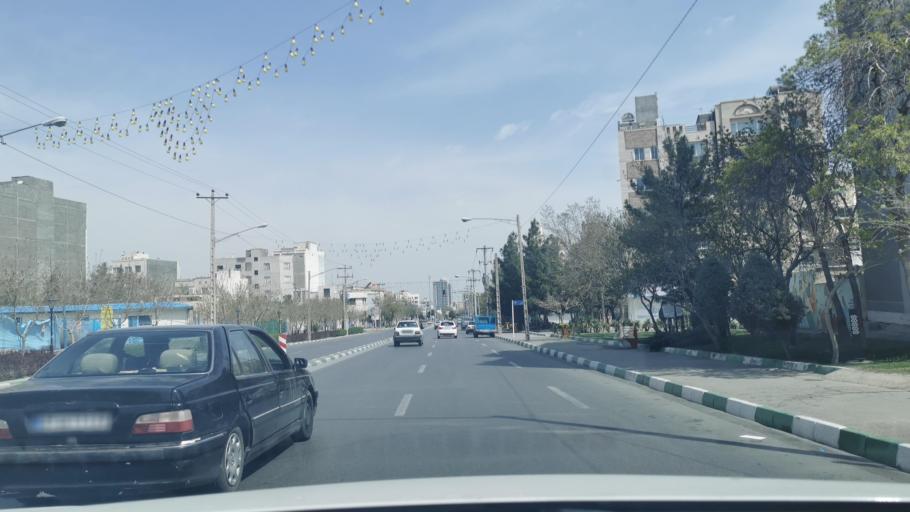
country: IR
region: Razavi Khorasan
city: Mashhad
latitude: 36.3016
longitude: 59.5109
